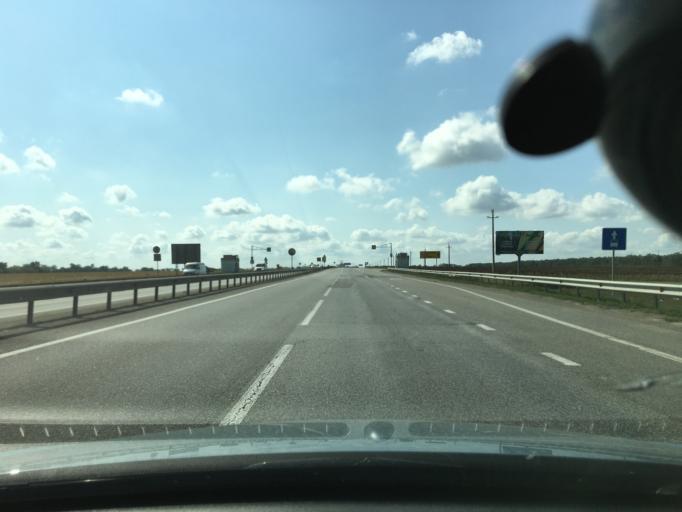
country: RU
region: Krasnodarskiy
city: Krasnoye
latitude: 46.7674
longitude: 39.6624
